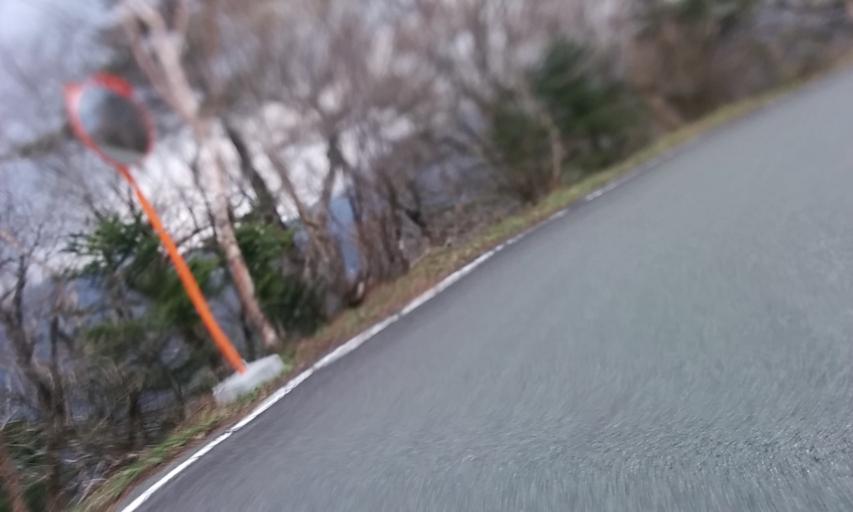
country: JP
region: Ehime
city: Saijo
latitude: 33.7828
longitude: 133.1915
